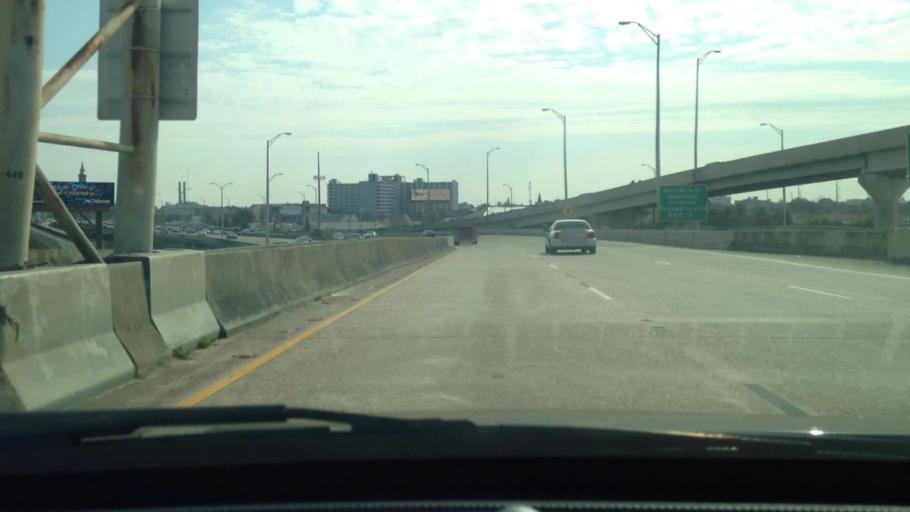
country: US
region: Louisiana
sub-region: Orleans Parish
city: New Orleans
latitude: 29.9498
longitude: -90.0848
